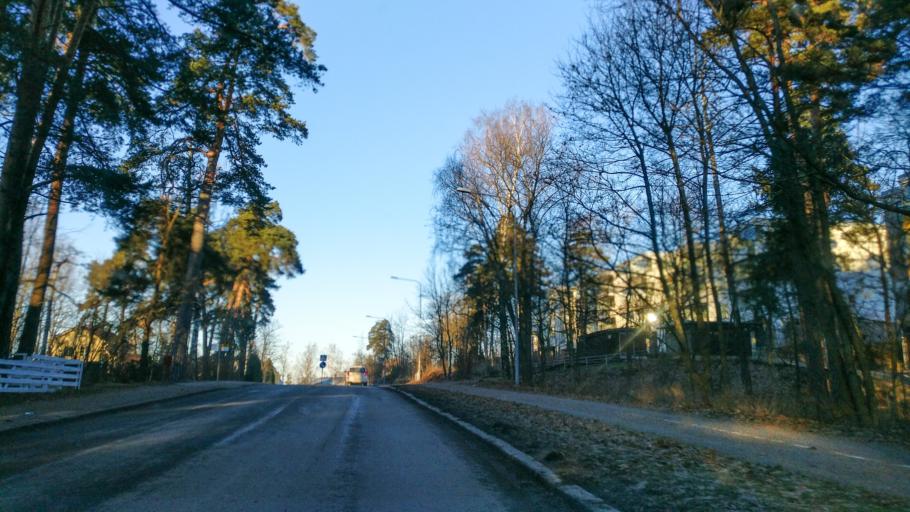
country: FI
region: Uusimaa
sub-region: Helsinki
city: Vantaa
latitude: 60.1821
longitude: 25.0508
